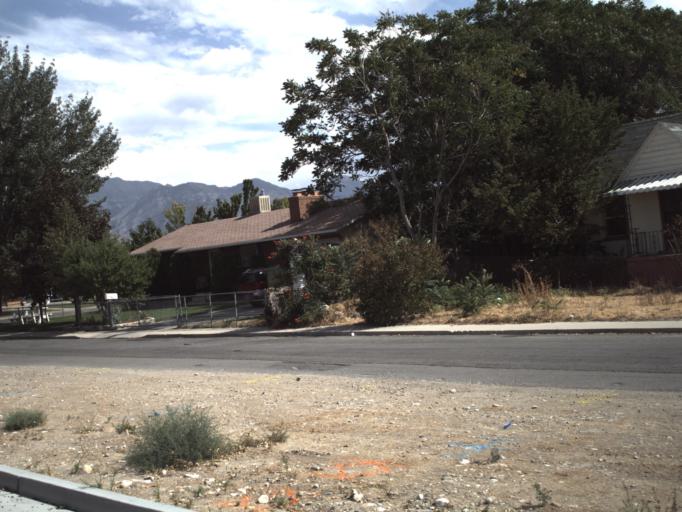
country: US
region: Utah
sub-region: Utah County
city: Orem
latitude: 40.3119
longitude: -111.7211
